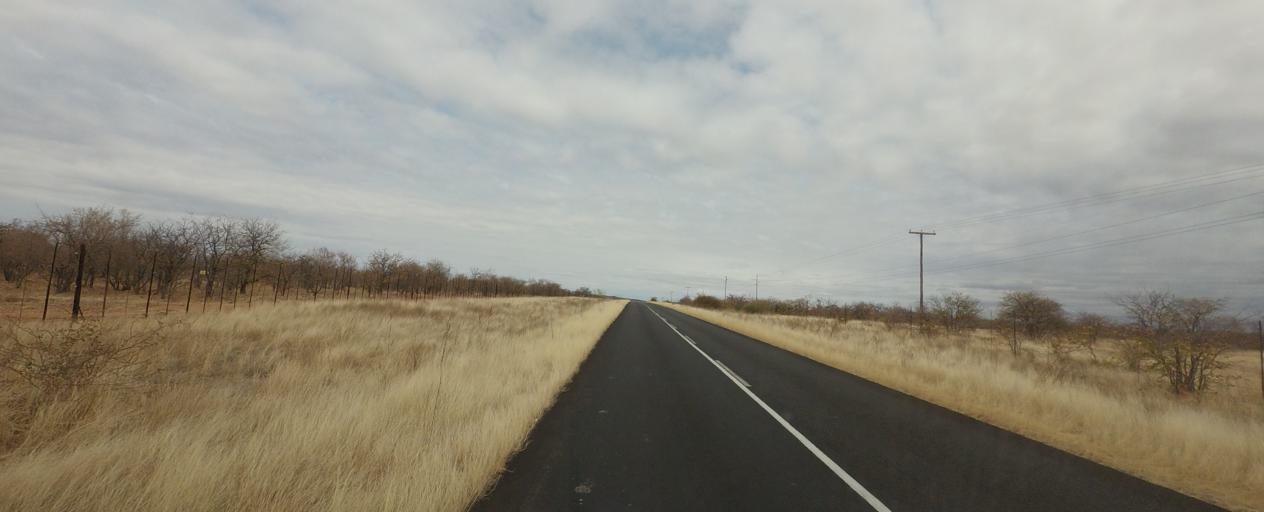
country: ZW
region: Matabeleland South
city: Beitbridge
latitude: -22.4308
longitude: 29.4523
